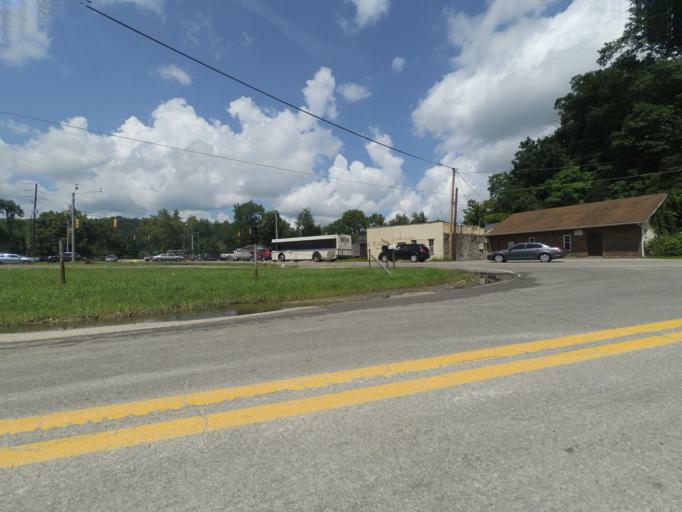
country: US
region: West Virginia
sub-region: Cabell County
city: Pea Ridge
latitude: 38.4120
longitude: -82.3608
